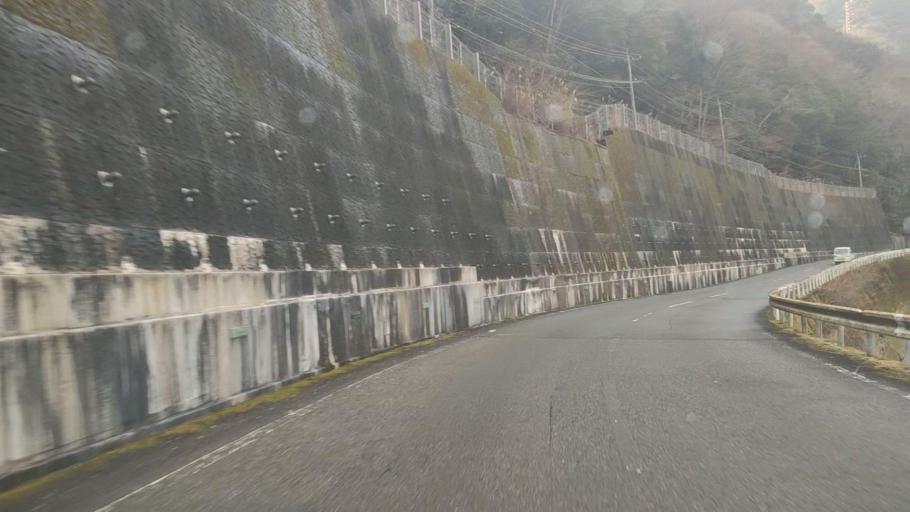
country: JP
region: Kumamoto
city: Hitoyoshi
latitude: 32.4217
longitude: 130.8554
